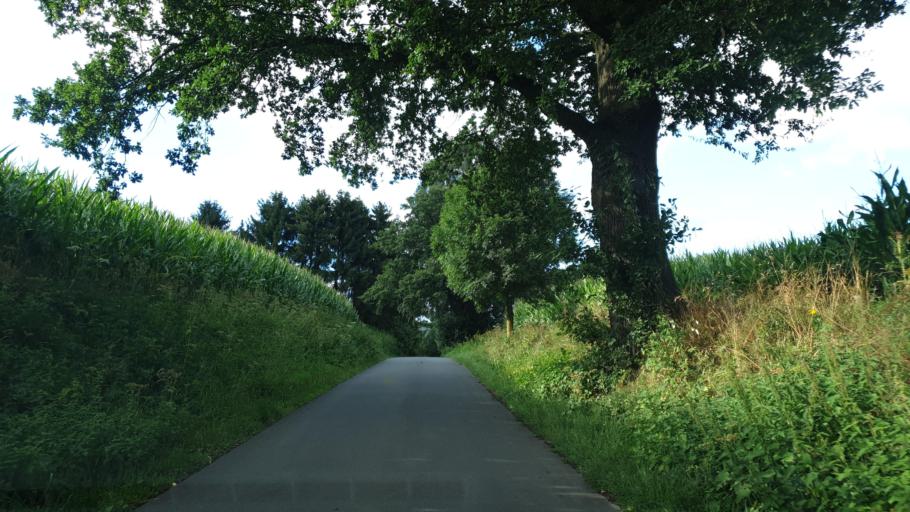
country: DE
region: North Rhine-Westphalia
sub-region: Regierungsbezirk Detmold
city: Huellhorst
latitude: 52.2688
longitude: 8.6897
